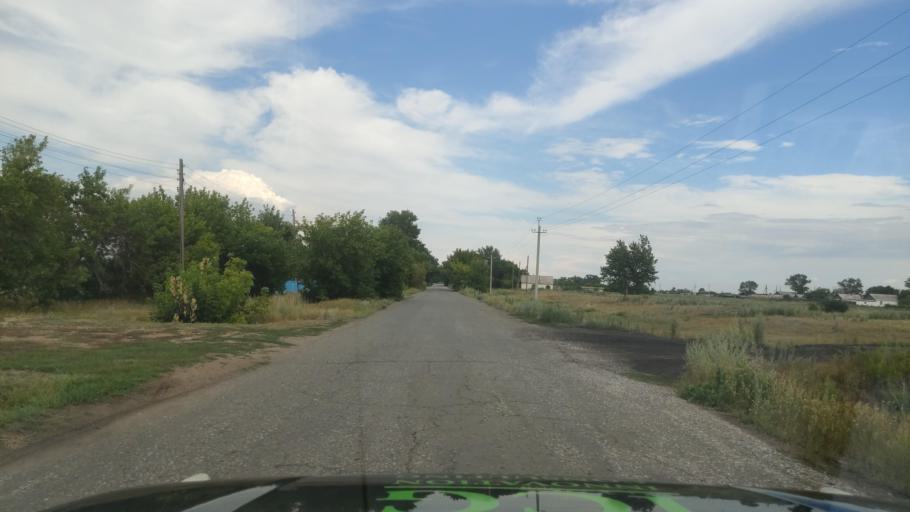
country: KZ
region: Pavlodar
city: Pavlodar
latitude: 52.6618
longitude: 77.5022
